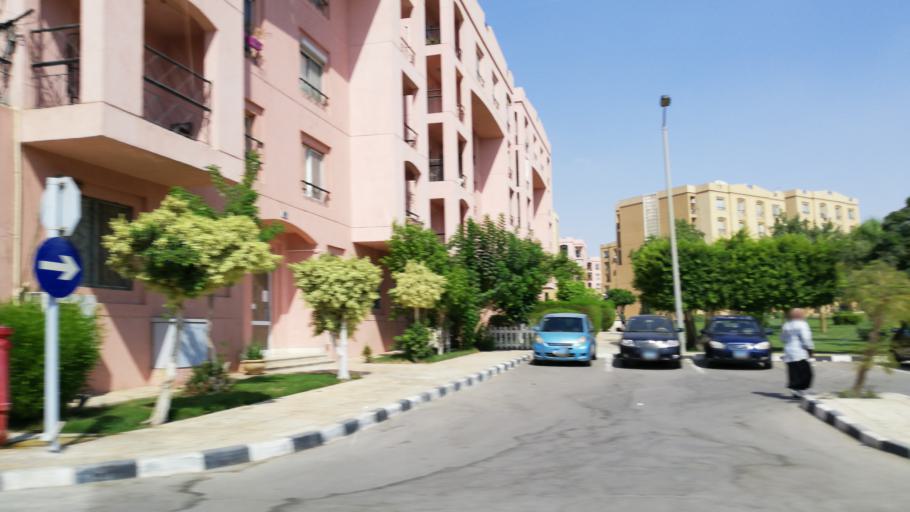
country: EG
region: Muhafazat al Qalyubiyah
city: Al Khankah
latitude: 30.0623
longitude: 31.4878
